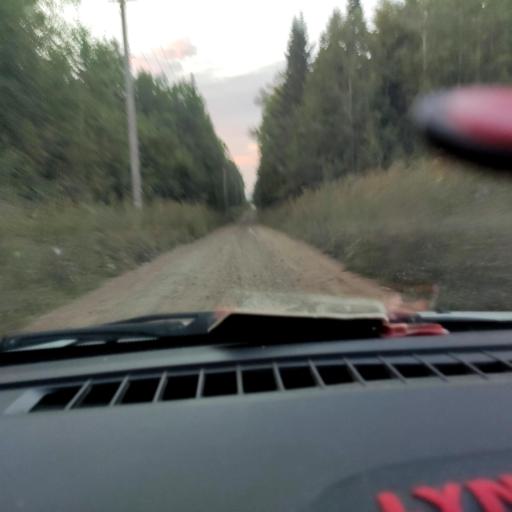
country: RU
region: Perm
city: Kukushtan
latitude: 57.6194
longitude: 56.4747
